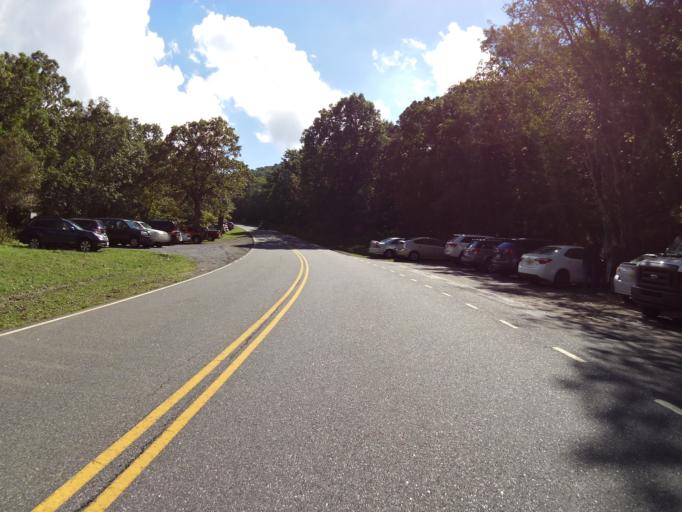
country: US
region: Virginia
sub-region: Page County
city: Stanley
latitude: 38.5564
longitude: -78.3867
